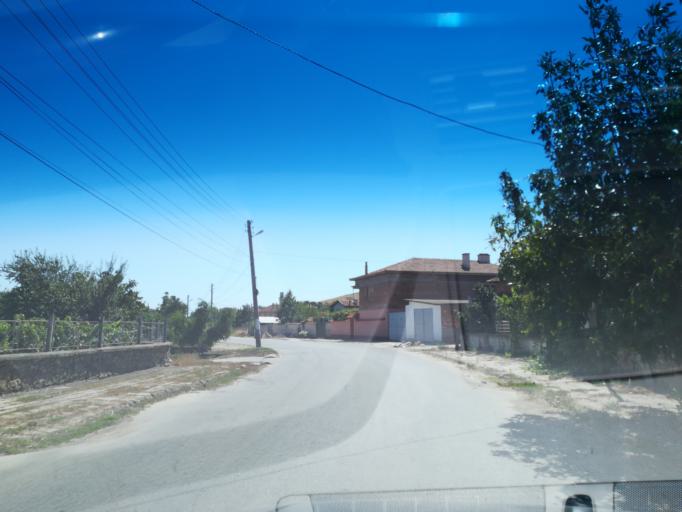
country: BG
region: Pazardzhik
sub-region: Obshtina Pazardzhik
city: Pazardzhik
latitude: 42.3309
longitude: 24.4024
